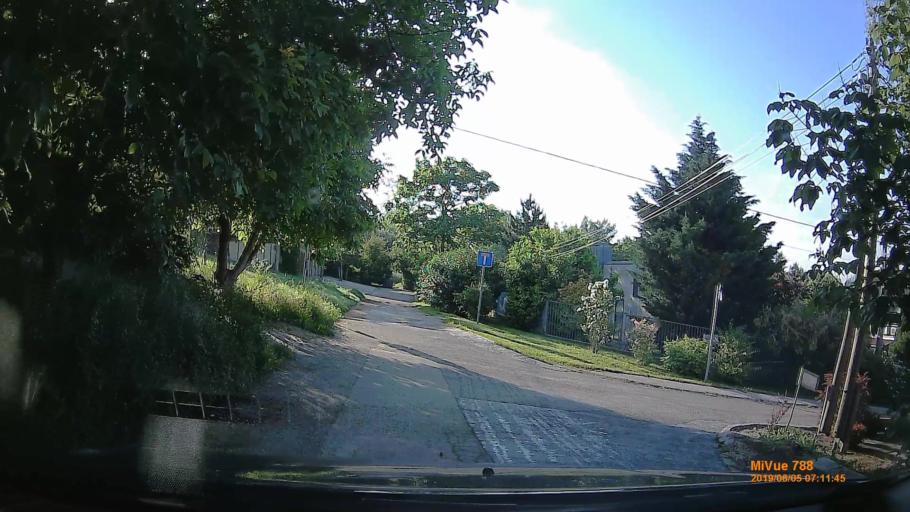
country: HU
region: Pest
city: Urom
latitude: 47.5832
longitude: 19.0312
